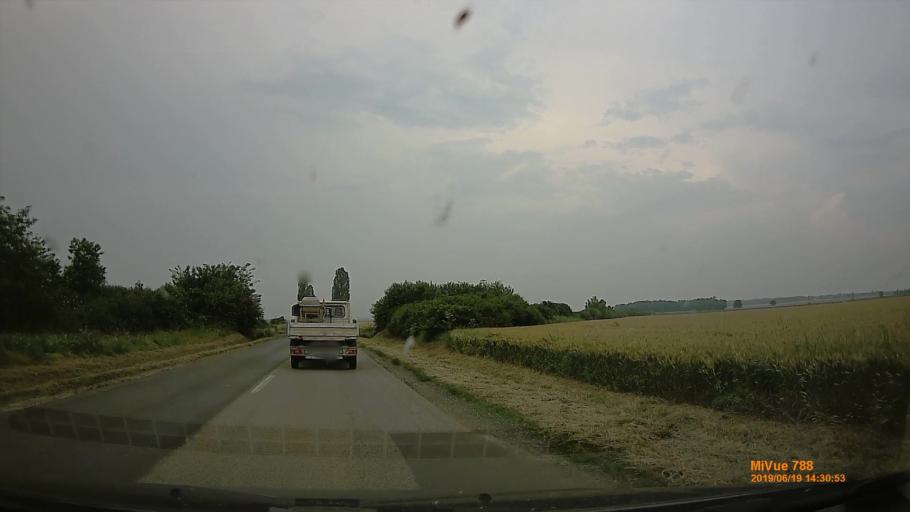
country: HU
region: Baranya
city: Szigetvar
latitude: 46.0669
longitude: 17.7698
